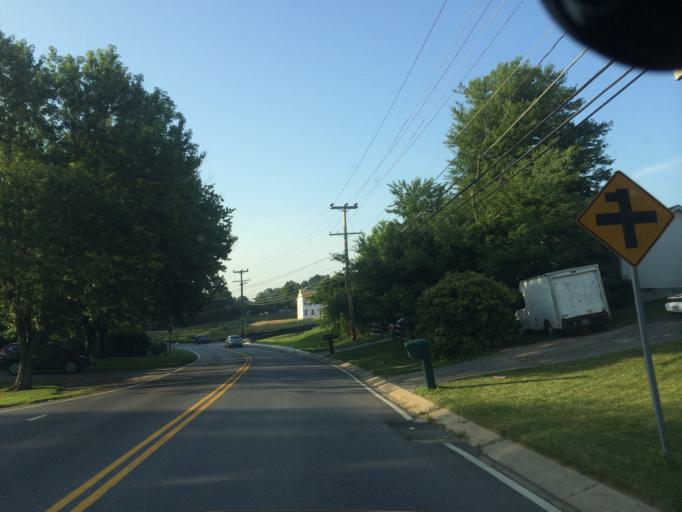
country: US
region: Maryland
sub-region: Carroll County
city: Eldersburg
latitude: 39.3916
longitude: -76.9306
